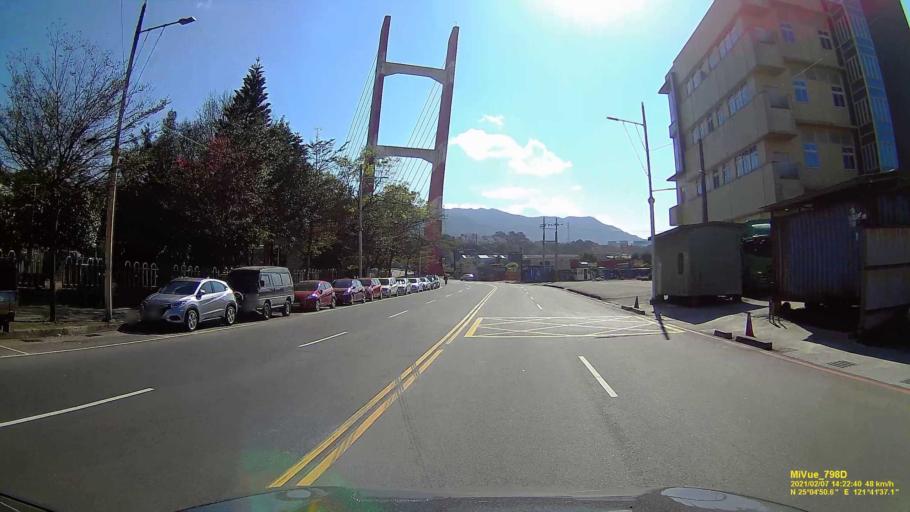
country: TW
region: Taiwan
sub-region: Keelung
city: Keelung
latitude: 25.0804
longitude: 121.6934
